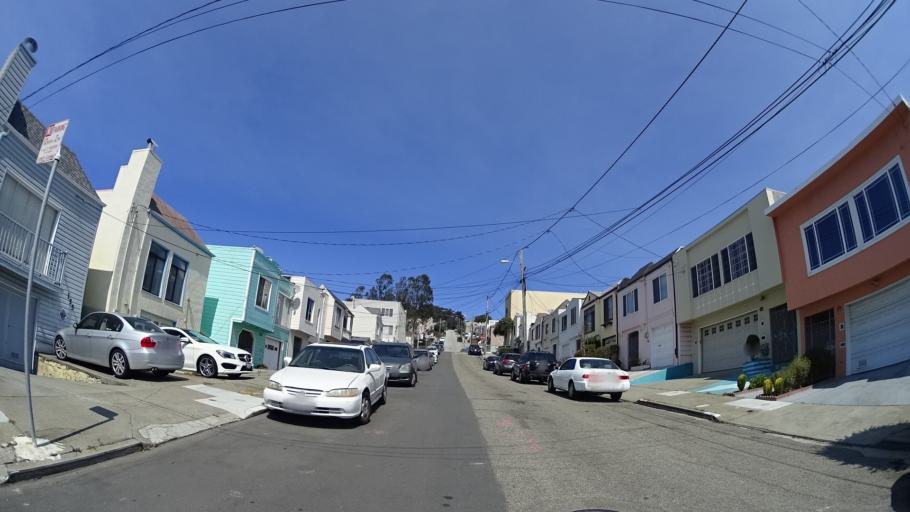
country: US
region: California
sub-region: San Mateo County
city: Daly City
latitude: 37.7135
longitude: -122.4662
